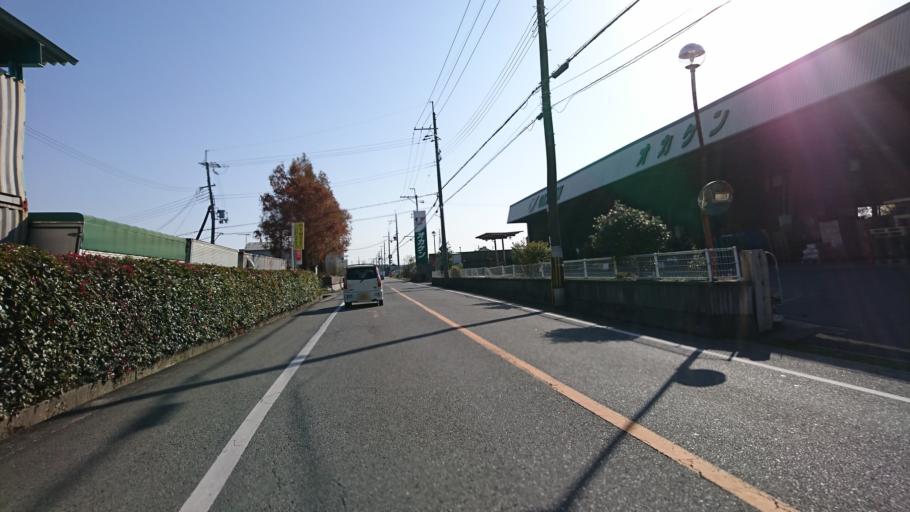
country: JP
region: Hyogo
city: Miki
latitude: 34.7612
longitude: 134.9469
